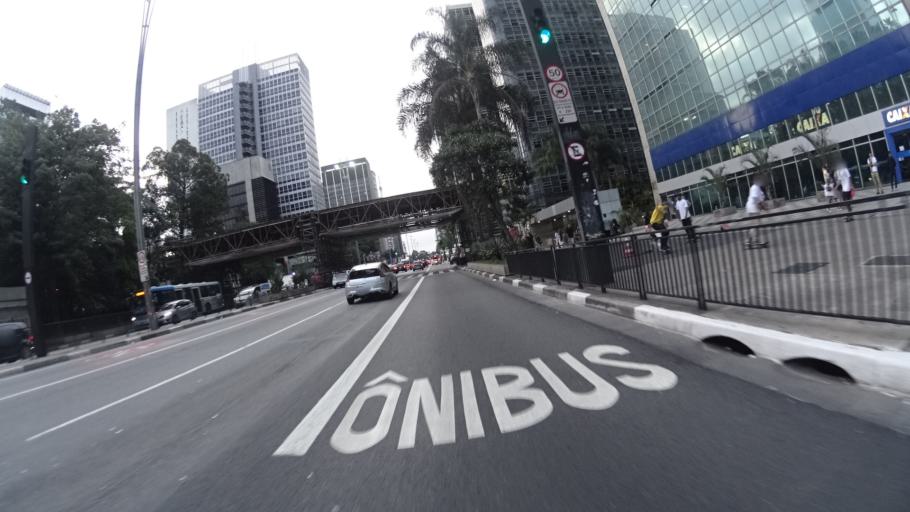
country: BR
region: Sao Paulo
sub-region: Sao Paulo
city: Sao Paulo
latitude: -23.5601
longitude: -46.6580
